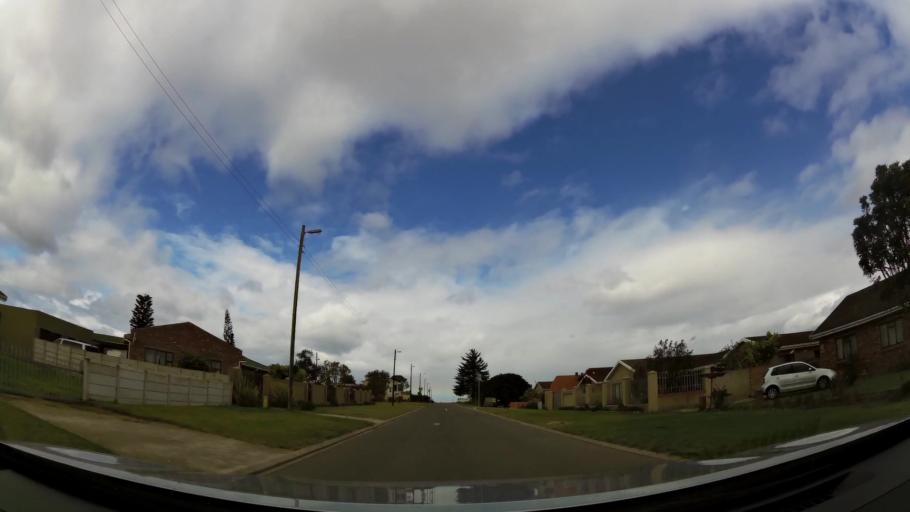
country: ZA
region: Western Cape
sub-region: Eden District Municipality
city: George
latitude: -34.0073
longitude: 22.4397
